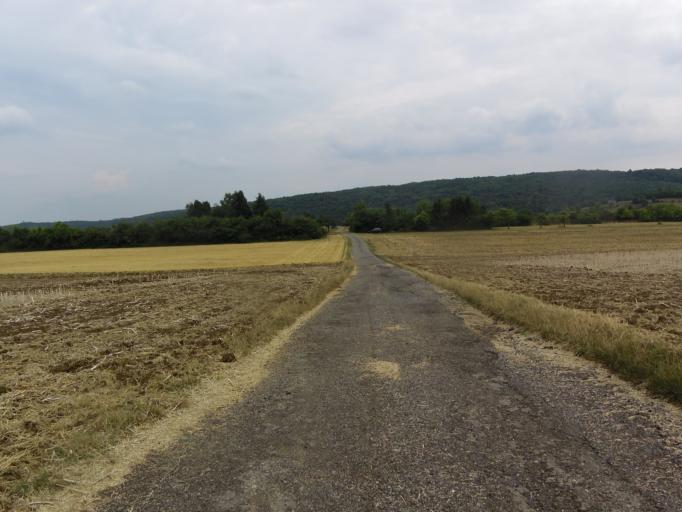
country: DE
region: Bavaria
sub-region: Regierungsbezirk Unterfranken
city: Hochberg
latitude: 49.7753
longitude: 9.8801
